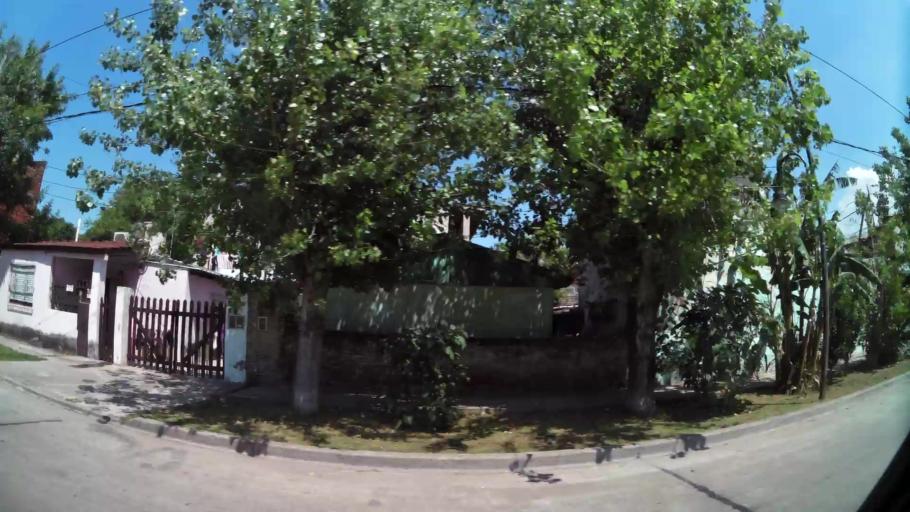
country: AR
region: Buenos Aires
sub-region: Partido de Tigre
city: Tigre
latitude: -34.4654
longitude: -58.5866
